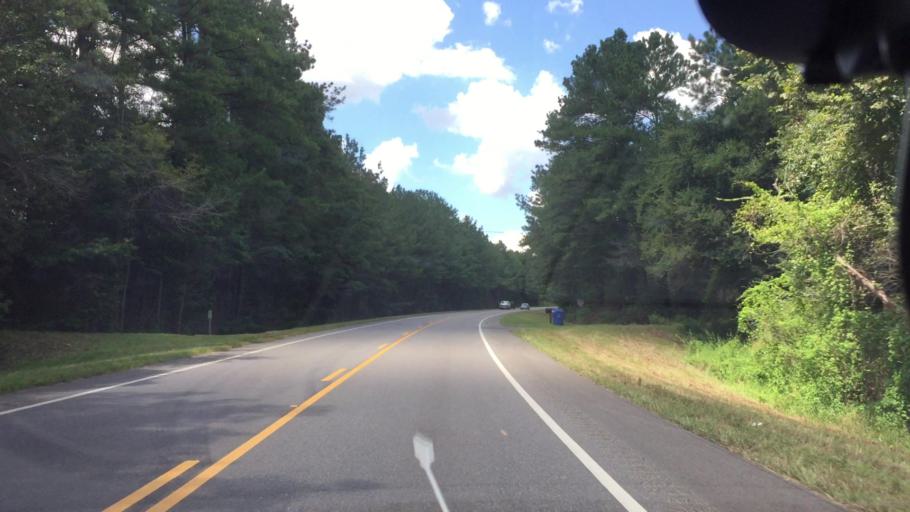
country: US
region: Alabama
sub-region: Pike County
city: Brundidge
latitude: 31.5944
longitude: -85.9450
